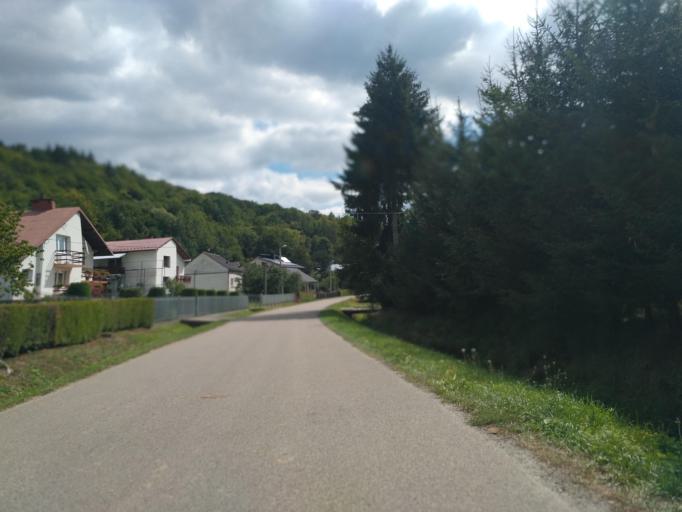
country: PL
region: Subcarpathian Voivodeship
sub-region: Powiat rzeszowski
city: Dynow
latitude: 49.7794
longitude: 22.2356
